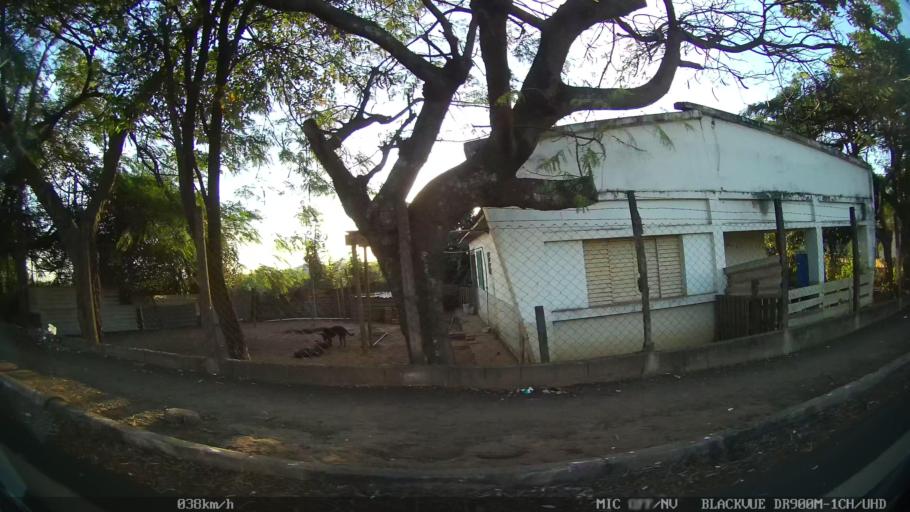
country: BR
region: Sao Paulo
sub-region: Franca
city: Franca
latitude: -20.5136
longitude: -47.4149
